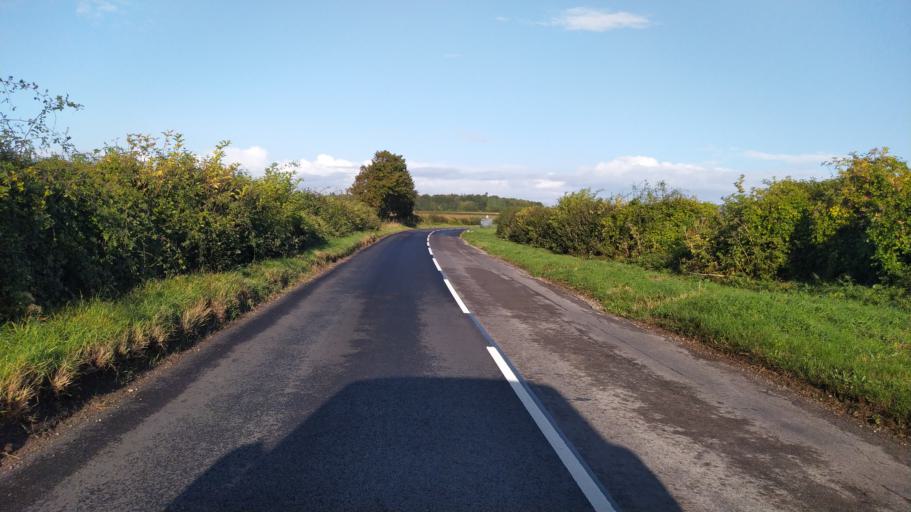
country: GB
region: England
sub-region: Dorset
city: Wimborne Minster
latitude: 50.8850
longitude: -1.9959
